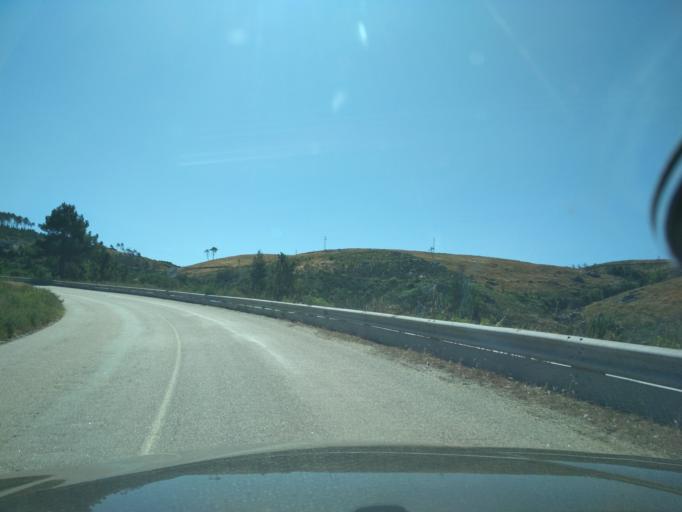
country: PT
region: Vila Real
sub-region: Ribeira de Pena
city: Ribeira de Pena
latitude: 41.5014
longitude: -7.7736
